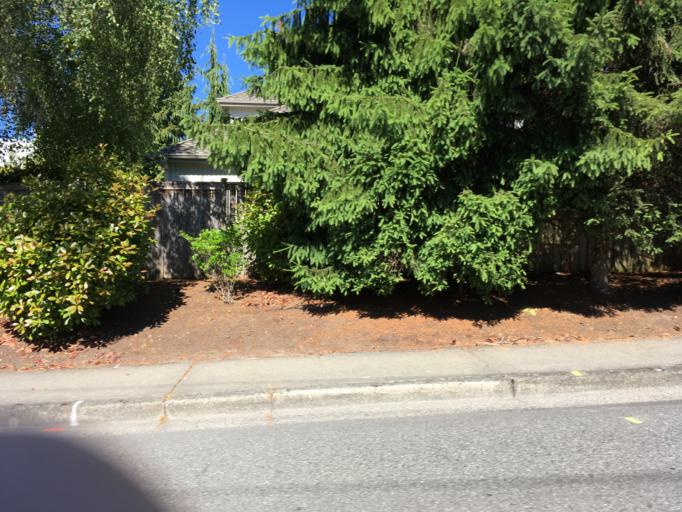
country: US
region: Washington
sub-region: King County
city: Clyde Hill
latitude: 47.6249
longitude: -122.2070
